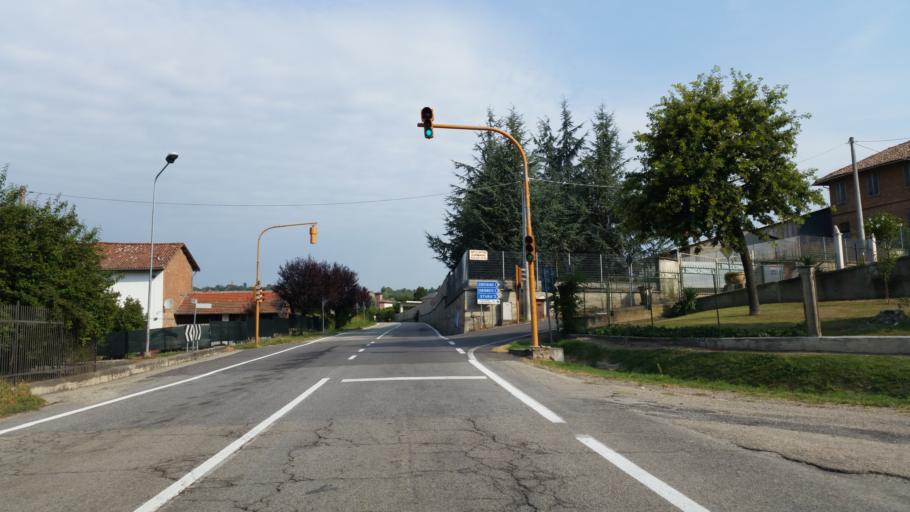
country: IT
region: Piedmont
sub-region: Provincia di Asti
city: Montiglio
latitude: 45.0657
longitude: 8.1121
